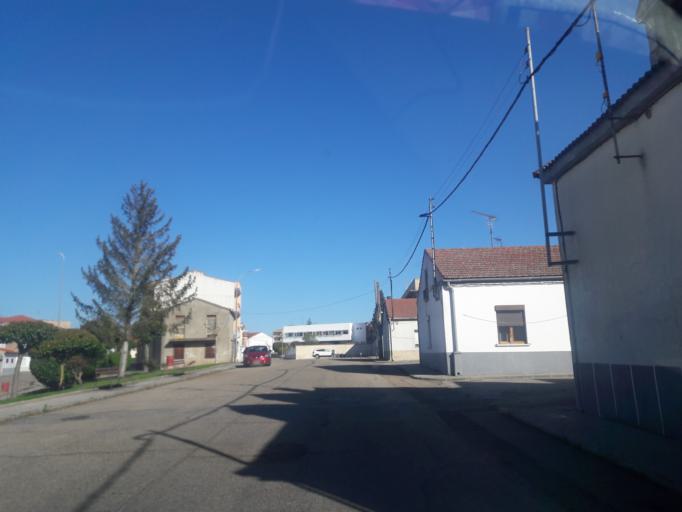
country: ES
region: Castille and Leon
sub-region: Provincia de Salamanca
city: Vitigudino
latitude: 41.0113
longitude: -6.4322
